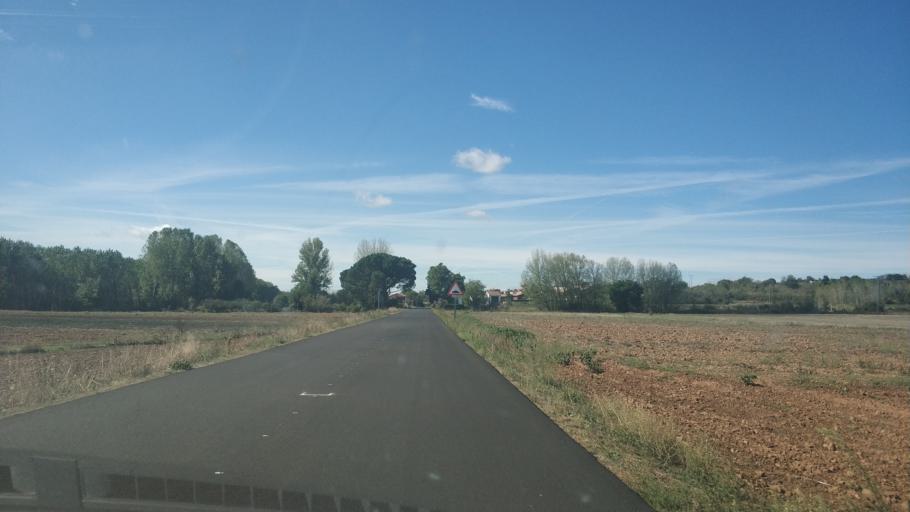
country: ES
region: Castille and Leon
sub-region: Provincia de Burgos
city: Puentedura
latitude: 42.0461
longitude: -3.5770
